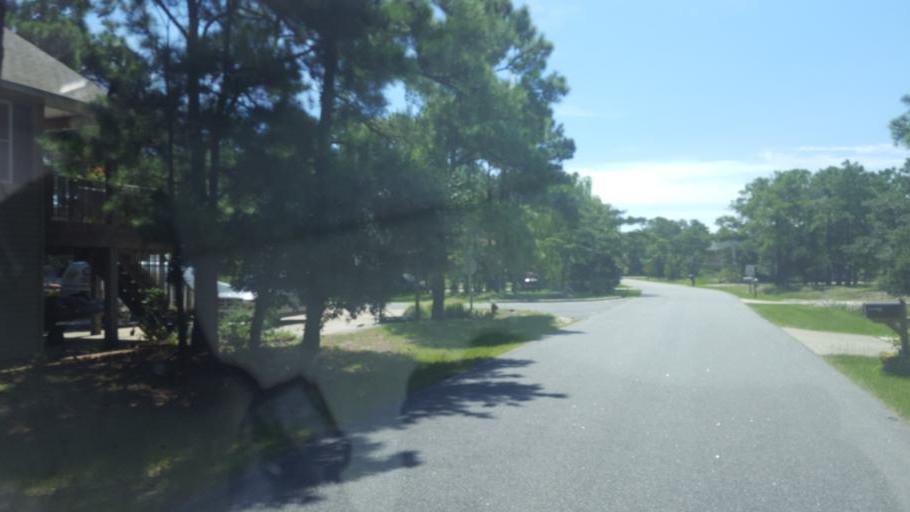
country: US
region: North Carolina
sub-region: Dare County
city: Kill Devil Hills
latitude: 35.9970
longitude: -75.6598
